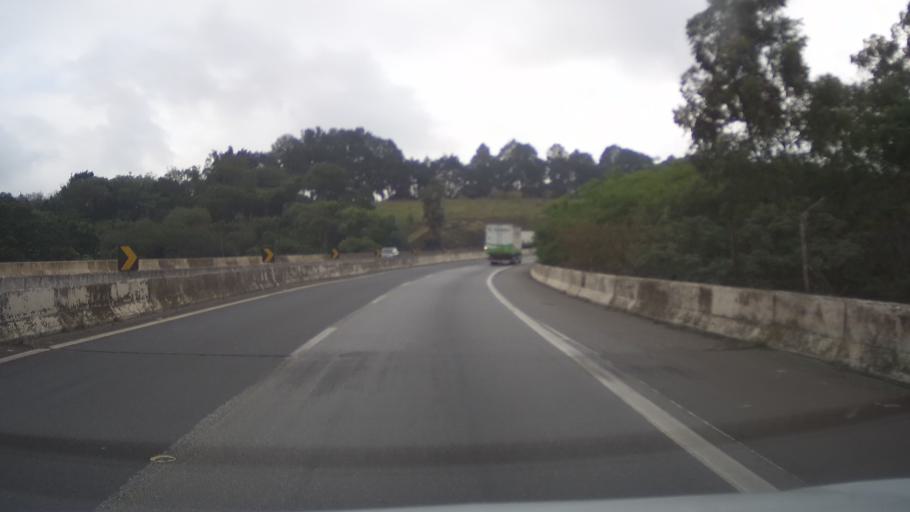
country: BR
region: Minas Gerais
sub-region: Extrema
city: Extrema
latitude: -22.8619
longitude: -46.3443
